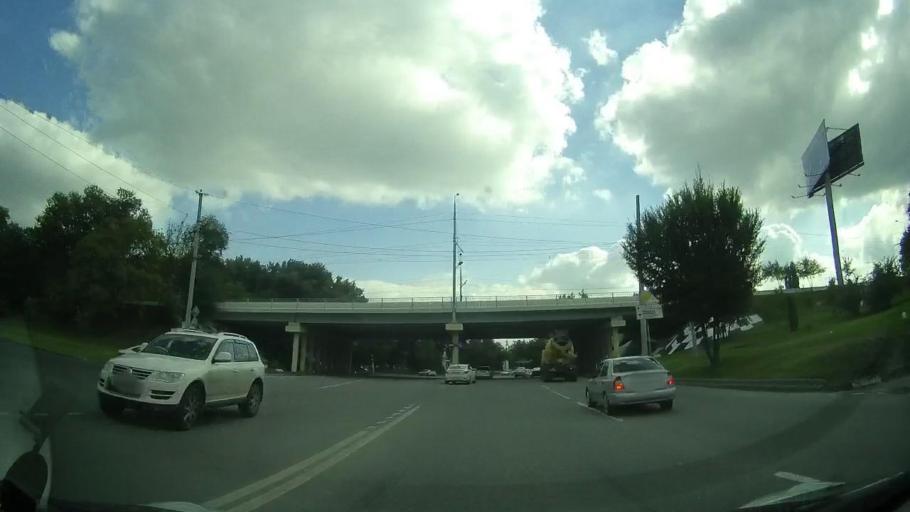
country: RU
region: Rostov
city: Imeni Chkalova
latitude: 47.2552
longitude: 39.7946
